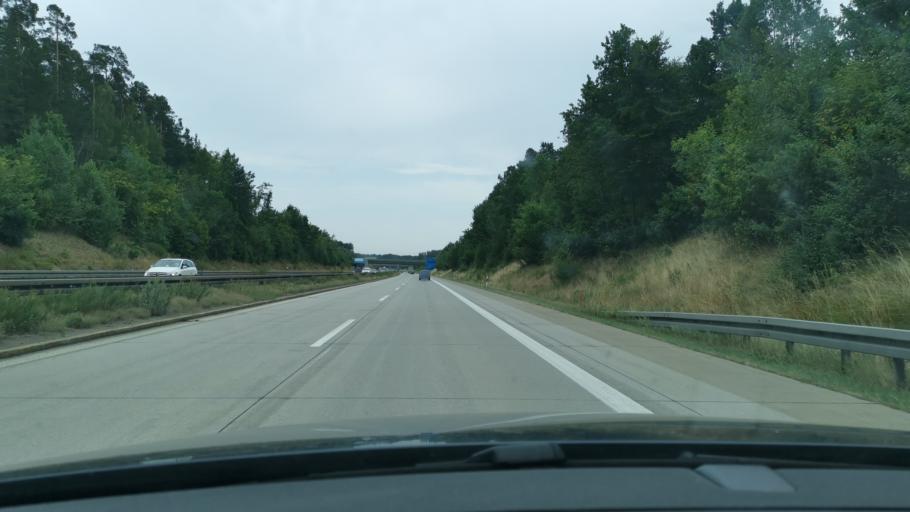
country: DE
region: Bavaria
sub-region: Upper Palatinate
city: Wernberg-Koblitz
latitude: 49.5456
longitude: 12.1289
